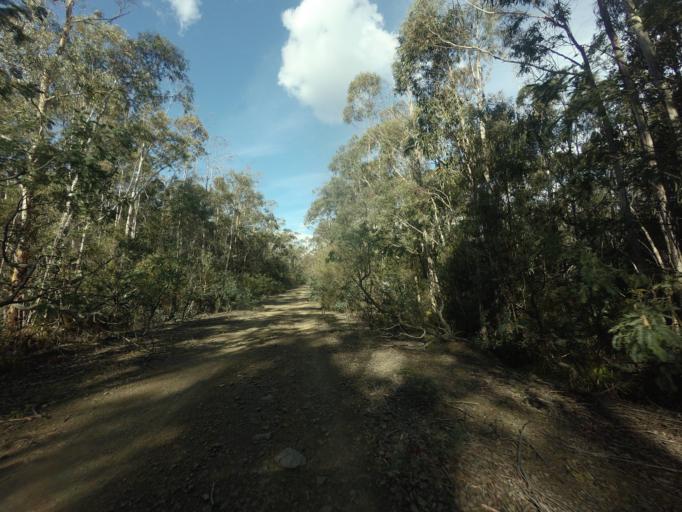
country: AU
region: Tasmania
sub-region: Break O'Day
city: St Helens
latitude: -41.8474
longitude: 148.0556
